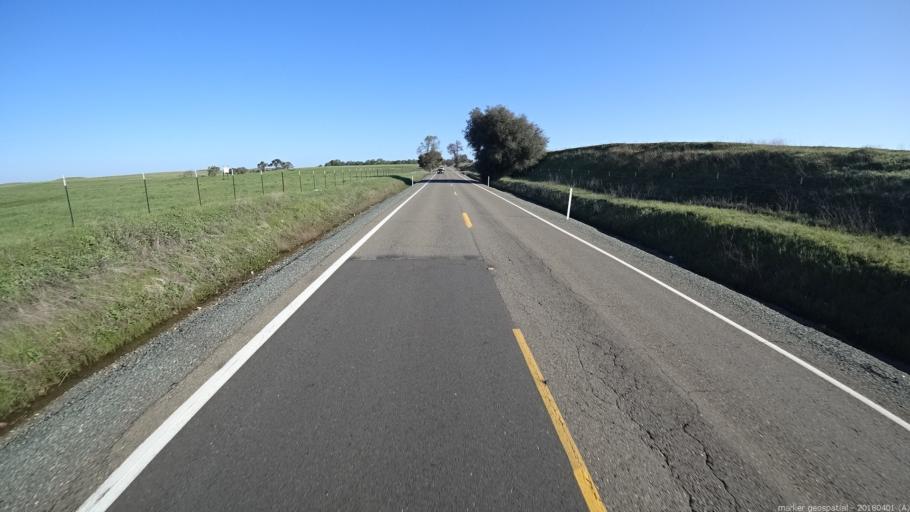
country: US
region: California
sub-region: Sacramento County
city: Rancho Murieta
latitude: 38.4717
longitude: -121.0440
